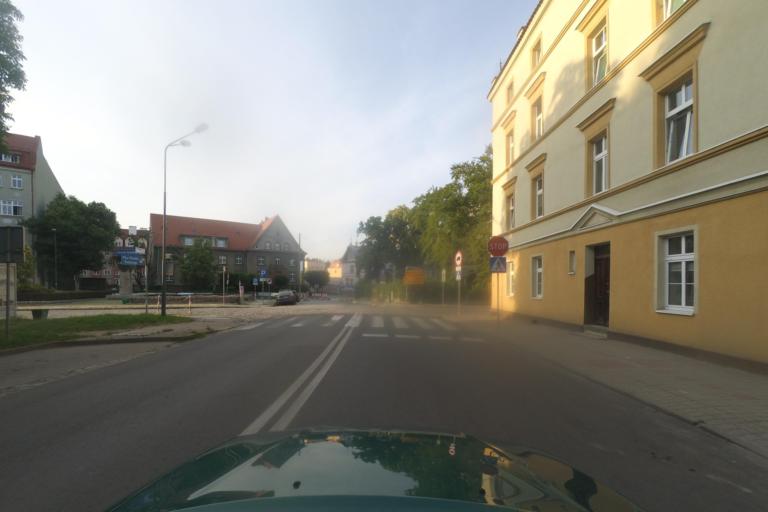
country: PL
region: Lower Silesian Voivodeship
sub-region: Powiat swidnicki
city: Swidnica
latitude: 50.8395
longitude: 16.4884
